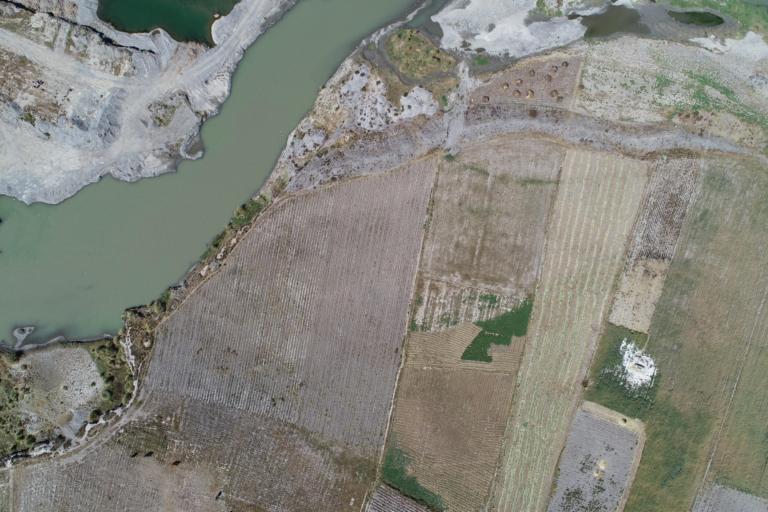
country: BO
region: La Paz
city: Achacachi
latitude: -16.0407
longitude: -68.6975
